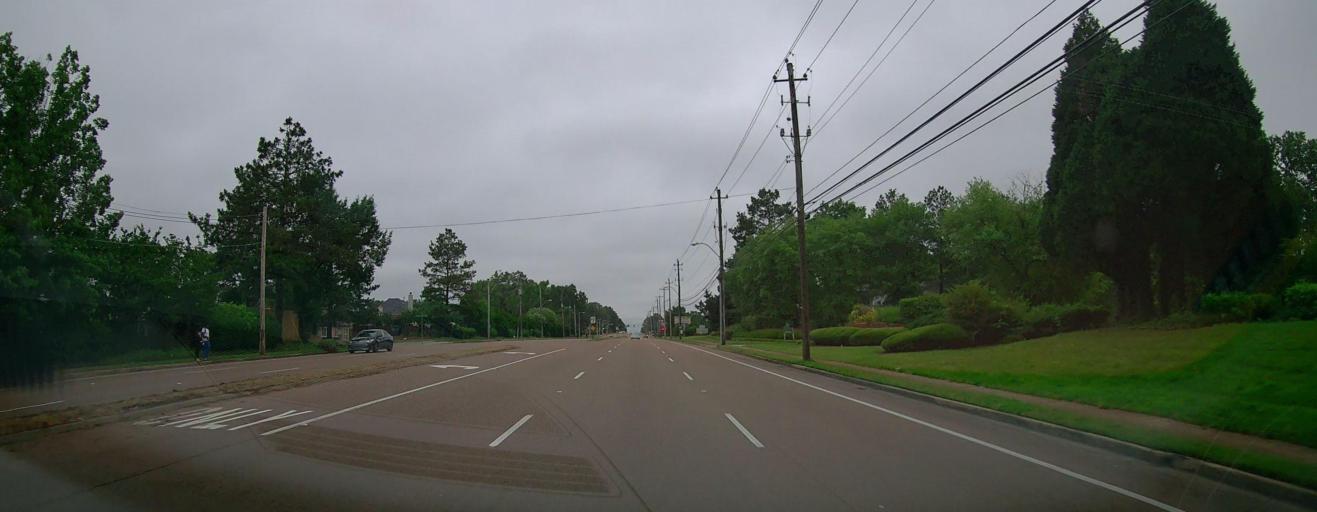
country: US
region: Tennessee
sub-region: Shelby County
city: Germantown
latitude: 35.0393
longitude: -89.8314
